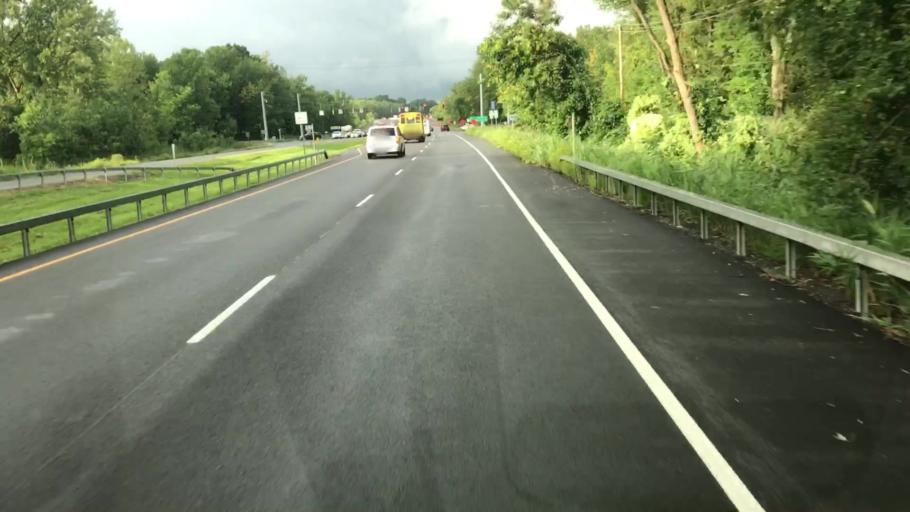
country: US
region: New York
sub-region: Onondaga County
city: Liverpool
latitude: 43.1262
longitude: -76.2444
